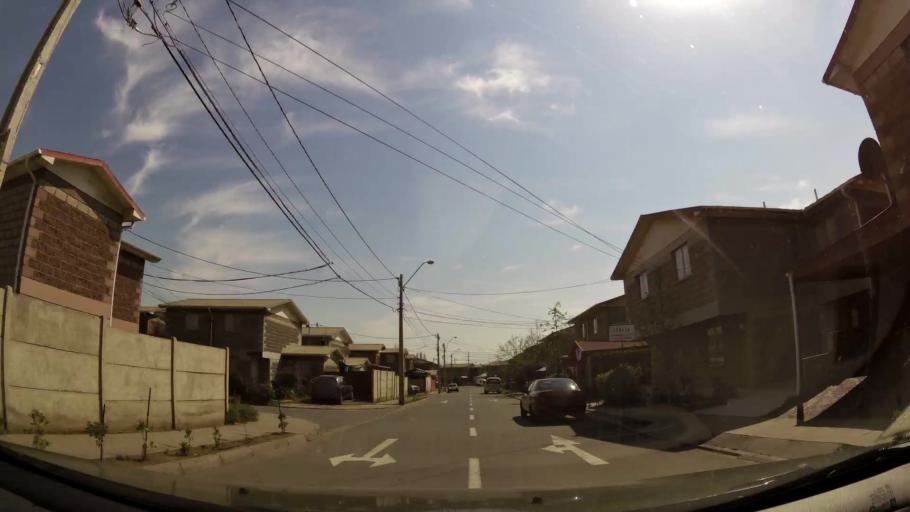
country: CL
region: Santiago Metropolitan
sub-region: Provincia de Santiago
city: La Pintana
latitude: -33.5691
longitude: -70.5987
